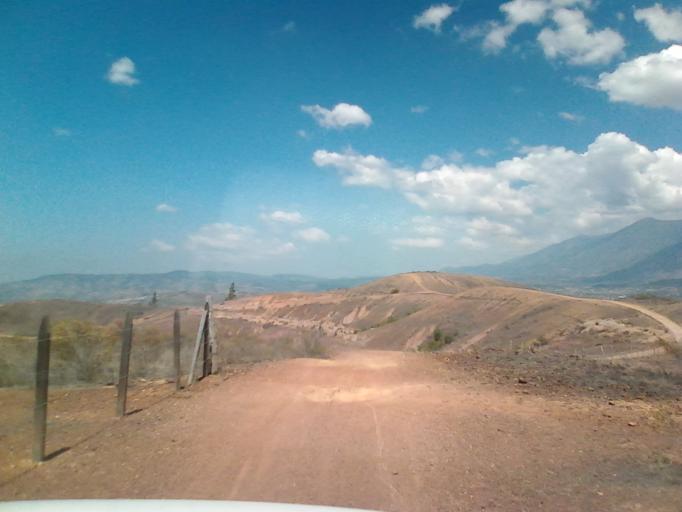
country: CO
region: Boyaca
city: Villa de Leiva
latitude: 5.6072
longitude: -73.5752
